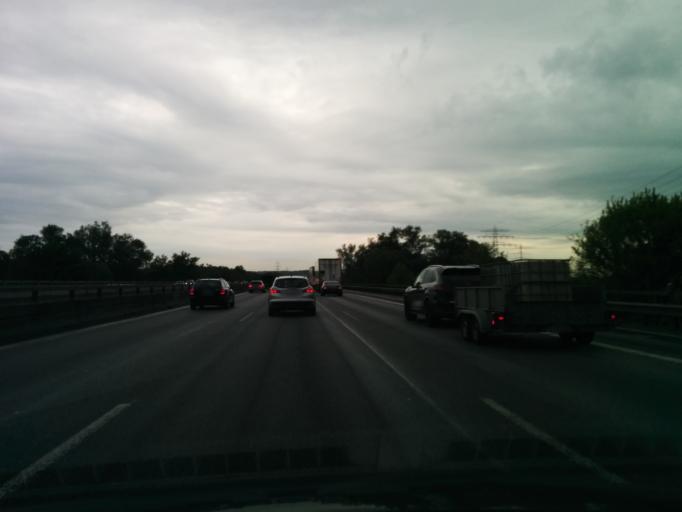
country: DE
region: Hamburg
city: Altona
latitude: 53.5022
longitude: 9.9124
